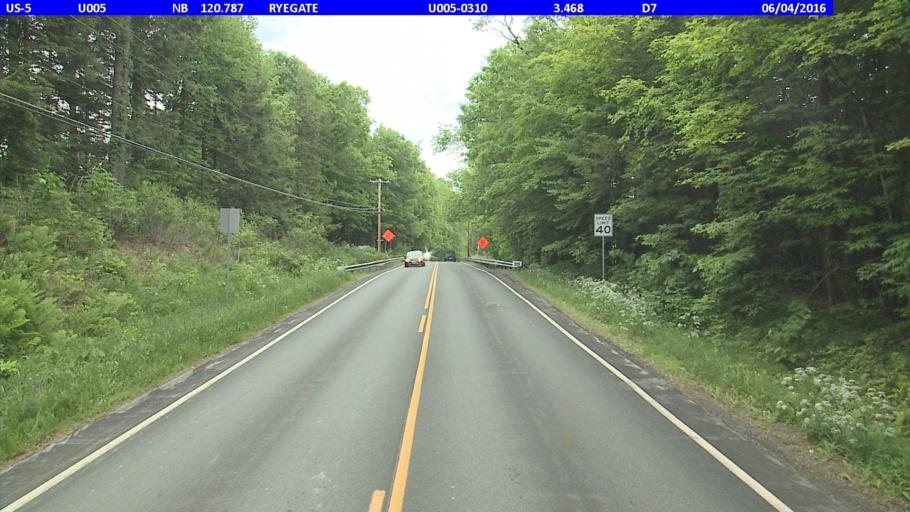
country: US
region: New Hampshire
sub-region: Grafton County
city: Woodsville
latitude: 44.2027
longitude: -72.0656
